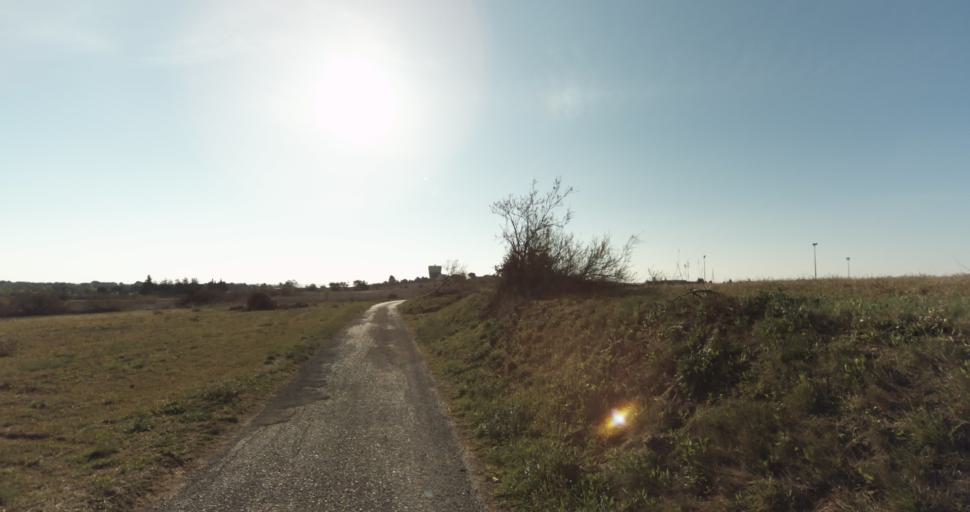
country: FR
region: Languedoc-Roussillon
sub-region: Departement de l'Herault
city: Marseillan
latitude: 43.3665
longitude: 3.5196
